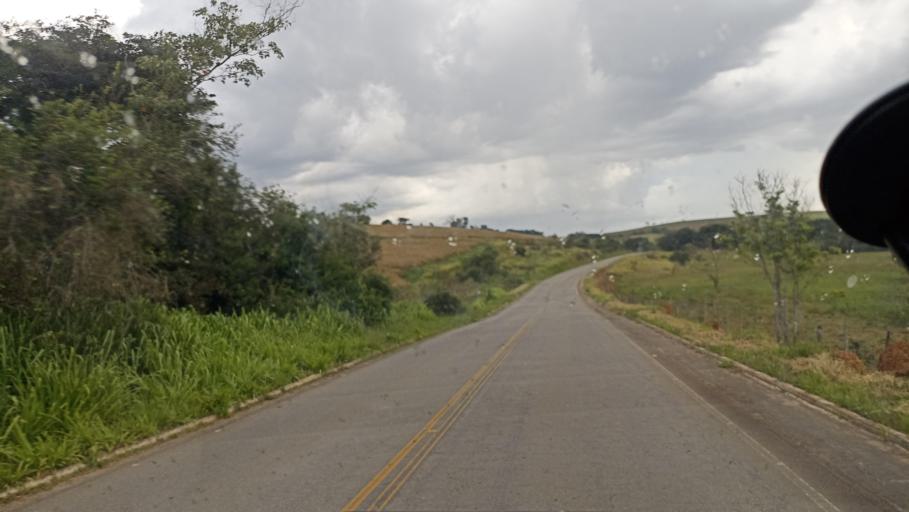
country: BR
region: Minas Gerais
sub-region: Cruzilia
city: Cruzilia
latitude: -21.9138
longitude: -44.8230
